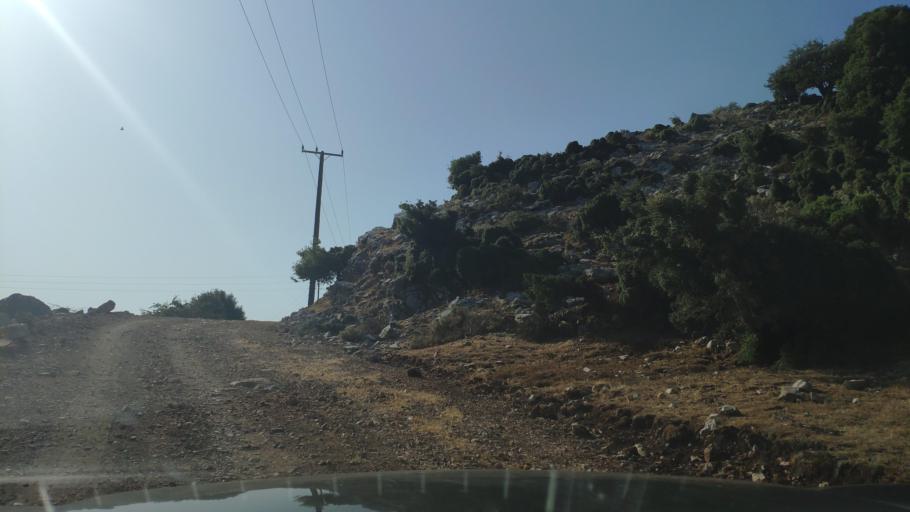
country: GR
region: West Greece
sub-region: Nomos Aitolias kai Akarnanias
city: Monastirakion
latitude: 38.8286
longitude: 20.9773
